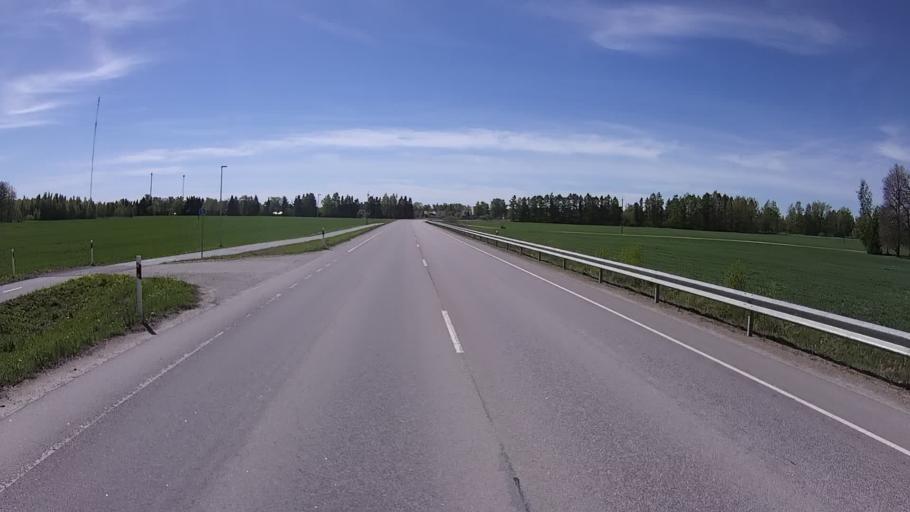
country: EE
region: Polvamaa
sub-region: Polva linn
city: Polva
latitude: 58.0754
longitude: 27.0884
